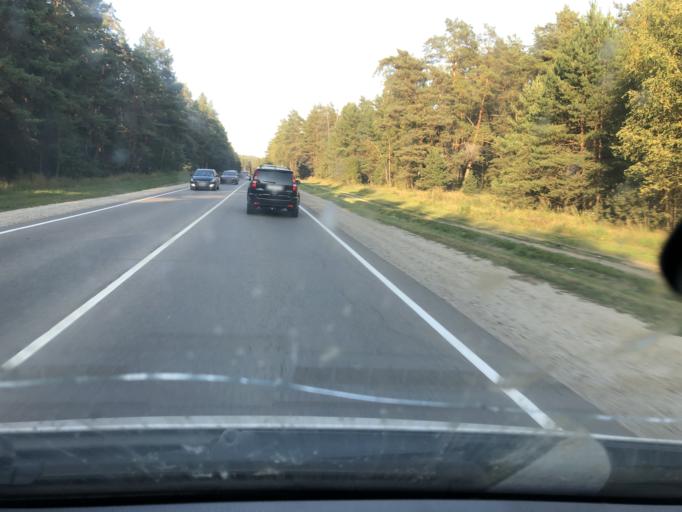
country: RU
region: Kaluga
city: Peremyshl'
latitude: 54.3515
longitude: 36.1956
